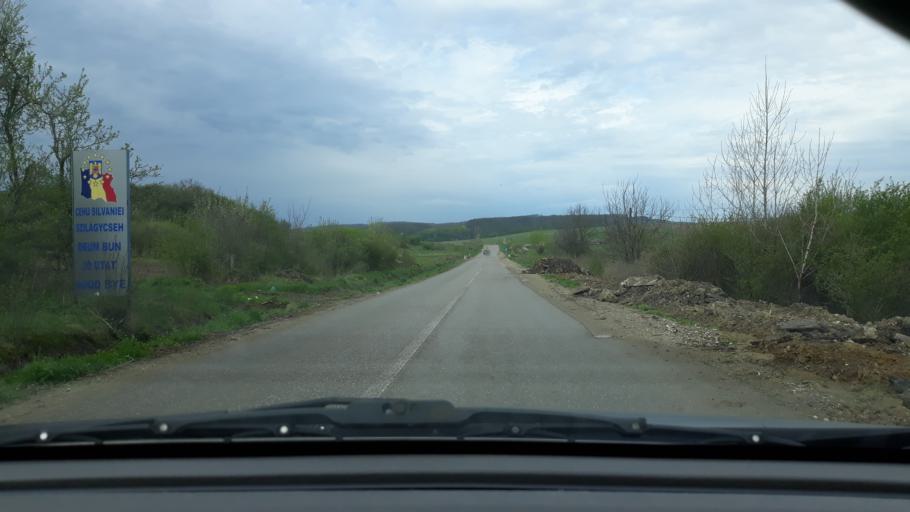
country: RO
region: Salaj
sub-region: Comuna Cehu Silvaniei
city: Cehu Silvaniei
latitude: 47.4027
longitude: 23.1602
